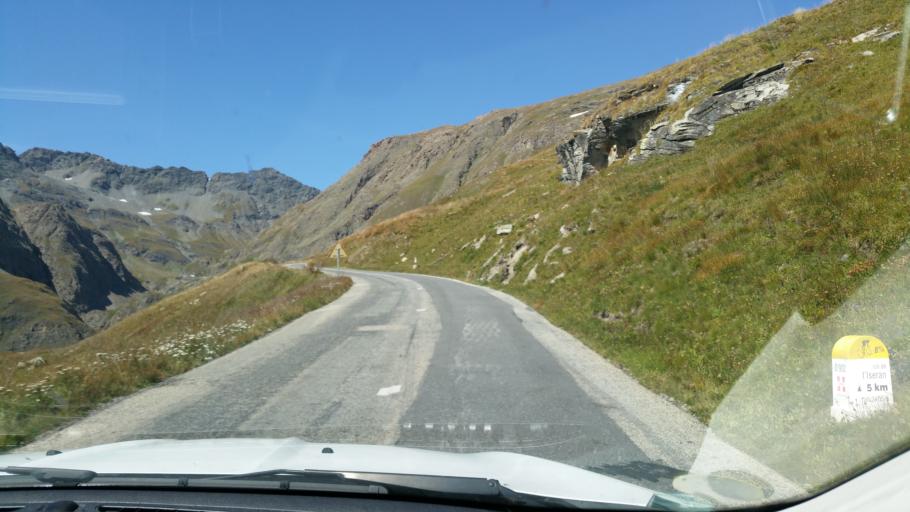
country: FR
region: Rhone-Alpes
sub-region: Departement de la Savoie
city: Val-d'Isere
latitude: 45.3926
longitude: 7.0452
